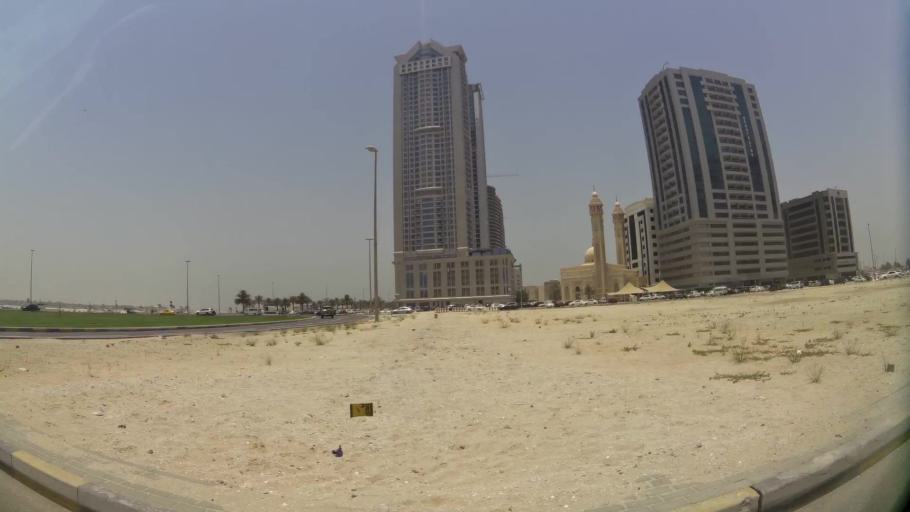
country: AE
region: Ash Shariqah
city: Sharjah
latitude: 25.3279
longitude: 55.3681
